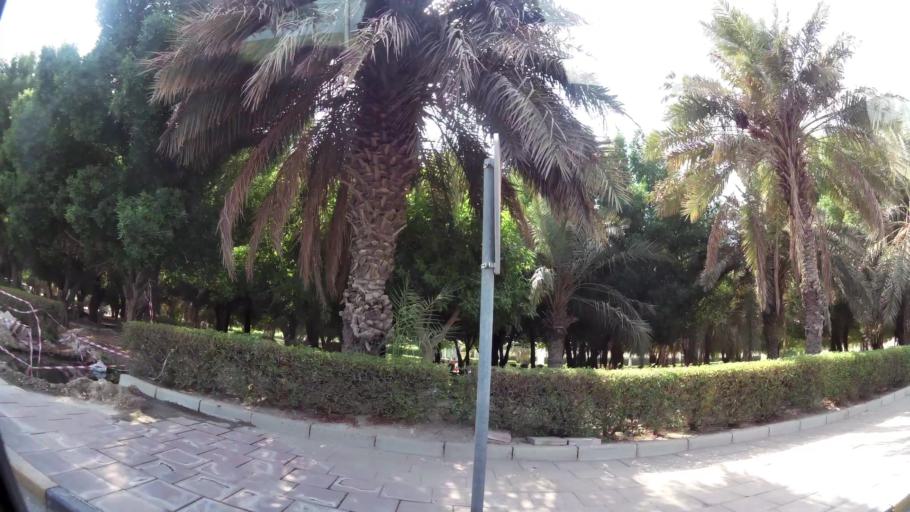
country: KW
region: Al Asimah
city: Ad Dasmah
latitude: 29.3591
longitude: 48.0251
